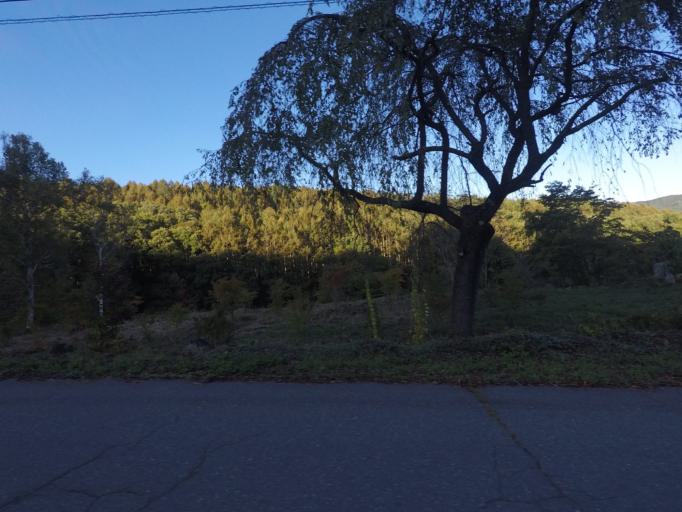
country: JP
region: Nagano
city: Ina
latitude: 35.9642
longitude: 137.7443
